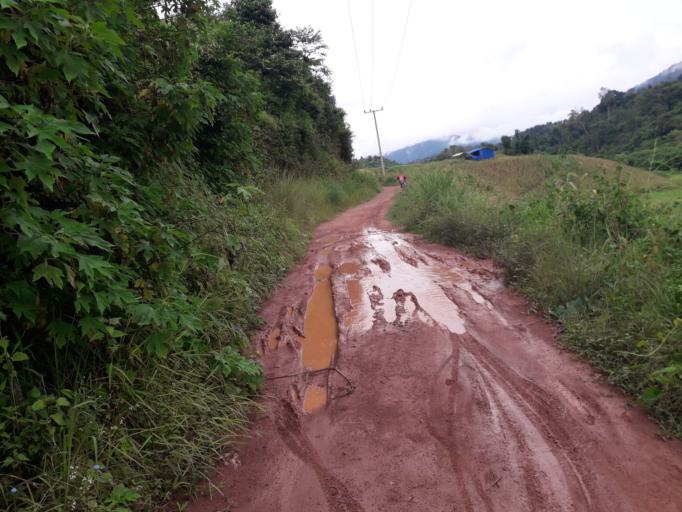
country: CN
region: Yunnan
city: Menglie
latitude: 22.2500
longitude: 101.6053
